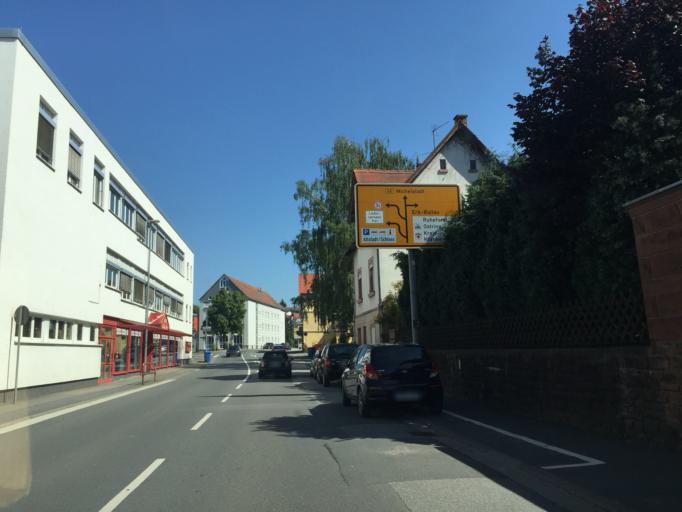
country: DE
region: Hesse
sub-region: Regierungsbezirk Darmstadt
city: Erbach
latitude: 49.6543
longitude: 8.9956
